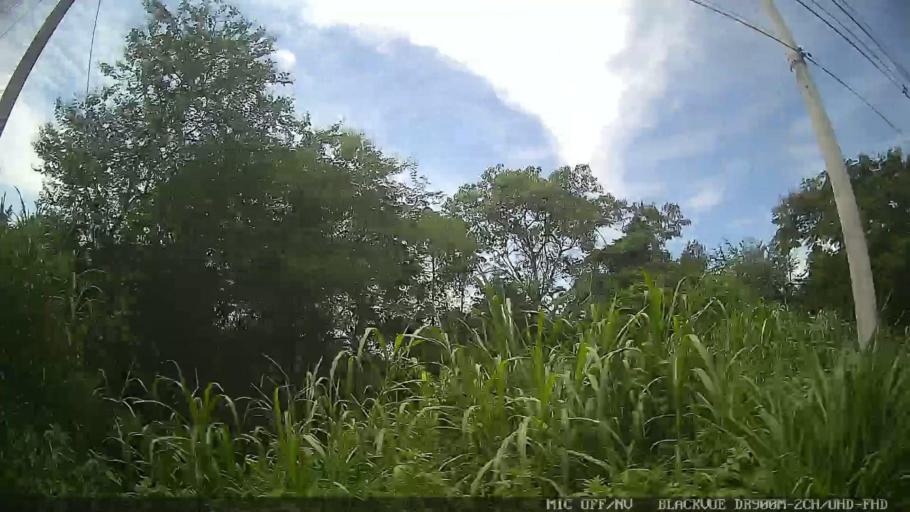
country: BR
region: Sao Paulo
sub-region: Aruja
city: Aruja
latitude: -23.4296
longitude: -46.2423
